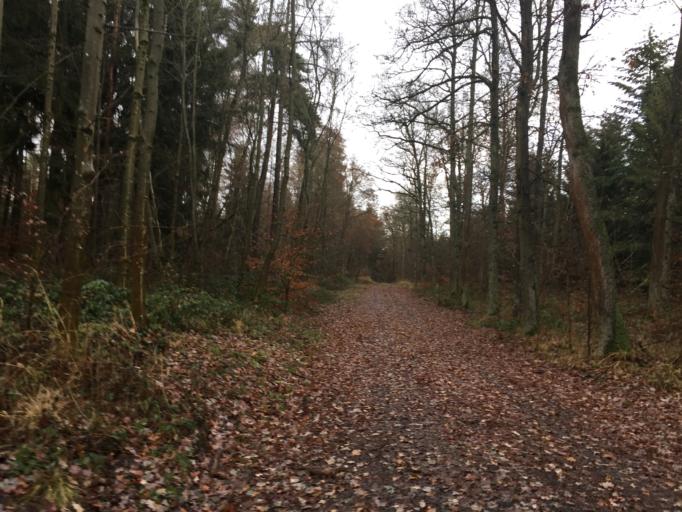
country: DE
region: Hesse
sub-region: Regierungsbezirk Giessen
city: Lich
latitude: 50.5364
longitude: 8.7867
